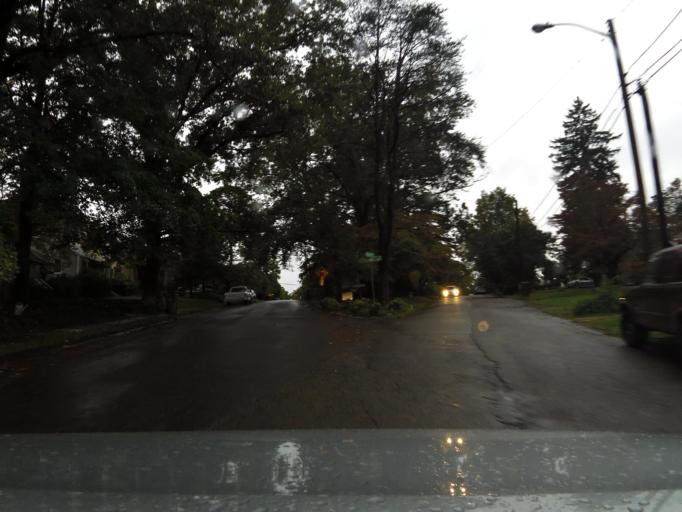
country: US
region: Tennessee
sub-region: Knox County
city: Knoxville
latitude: 35.9952
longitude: -83.9262
